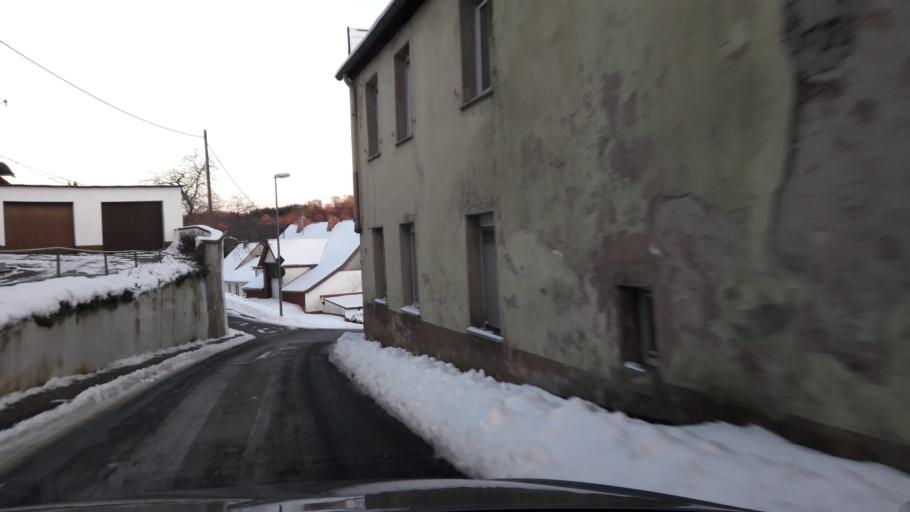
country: DE
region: Rheinland-Pfalz
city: Leitzweiler
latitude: 49.5913
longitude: 7.2214
